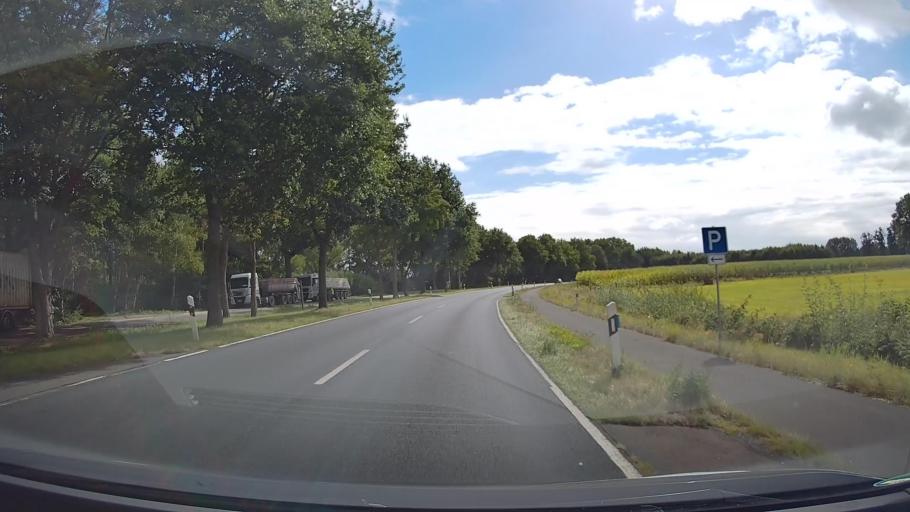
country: DE
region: Lower Saxony
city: Rhade
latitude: 53.3377
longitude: 9.1062
